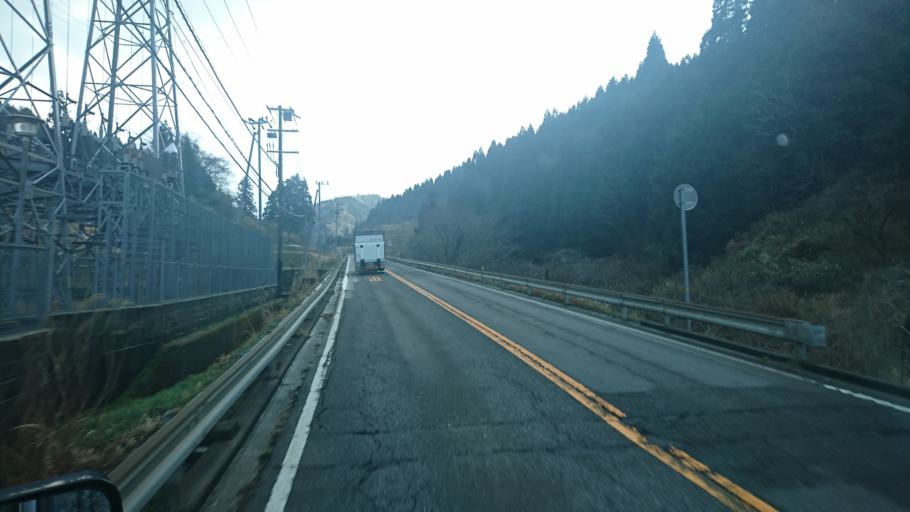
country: JP
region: Tottori
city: Tottori
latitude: 35.5421
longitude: 134.5068
